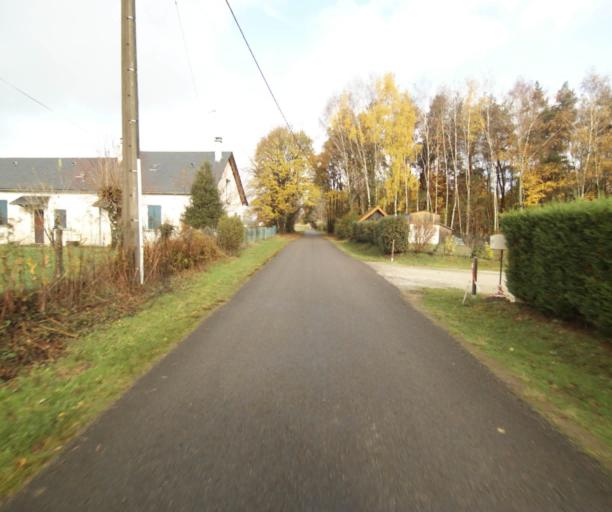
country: FR
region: Limousin
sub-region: Departement de la Correze
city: Sainte-Fereole
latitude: 45.2337
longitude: 1.6341
